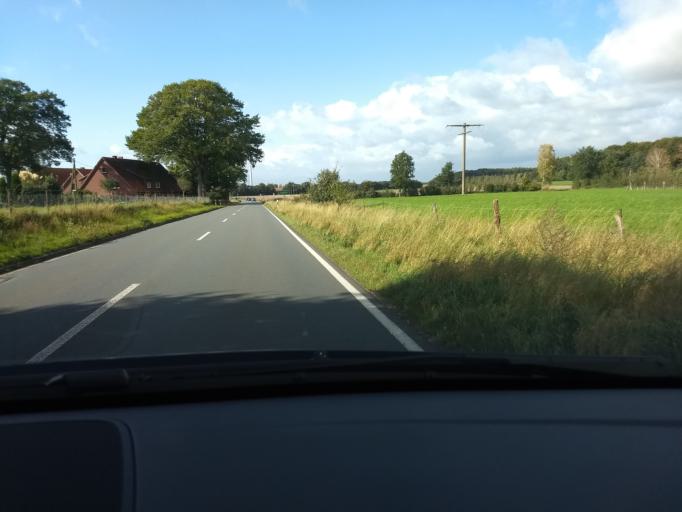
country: DE
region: North Rhine-Westphalia
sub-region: Regierungsbezirk Munster
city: Heiden
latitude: 51.8103
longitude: 6.9743
